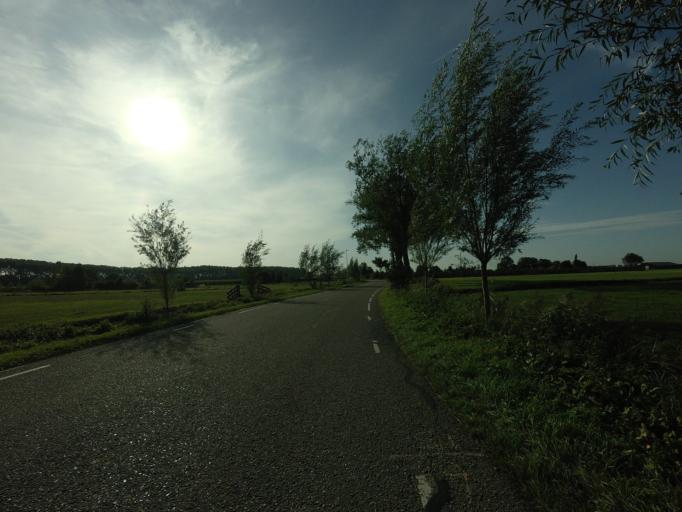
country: NL
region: Utrecht
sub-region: Gemeente Lopik
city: Lopik
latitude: 51.9449
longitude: 4.9691
